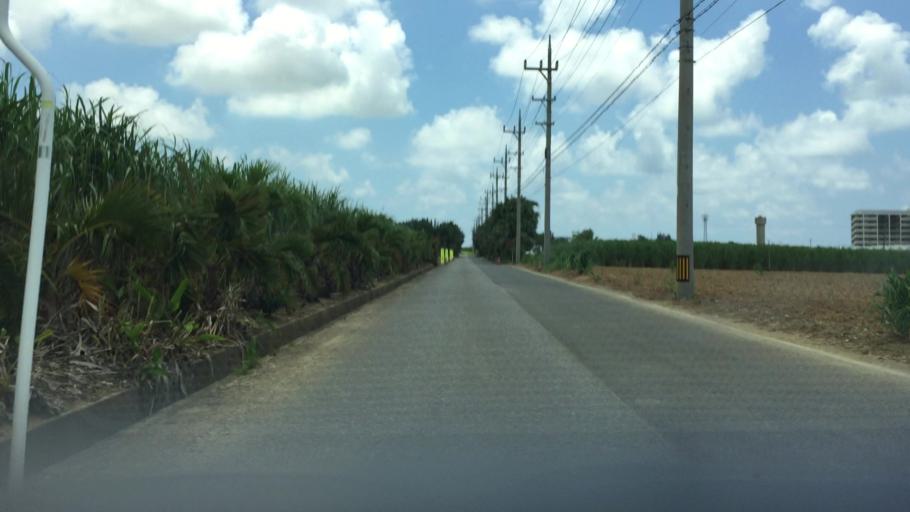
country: JP
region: Okinawa
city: Ishigaki
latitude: 24.3596
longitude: 124.1403
